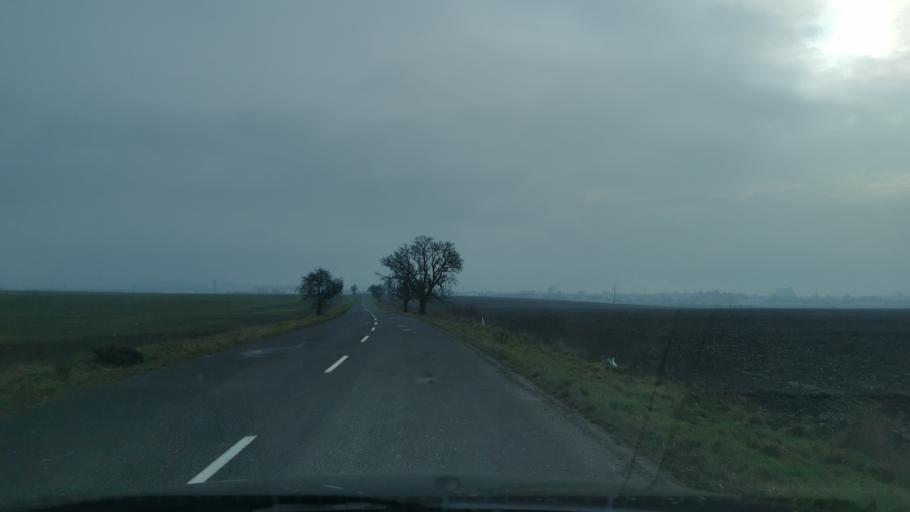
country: SK
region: Trnavsky
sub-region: Okres Senica
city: Senica
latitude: 48.6986
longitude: 17.3471
